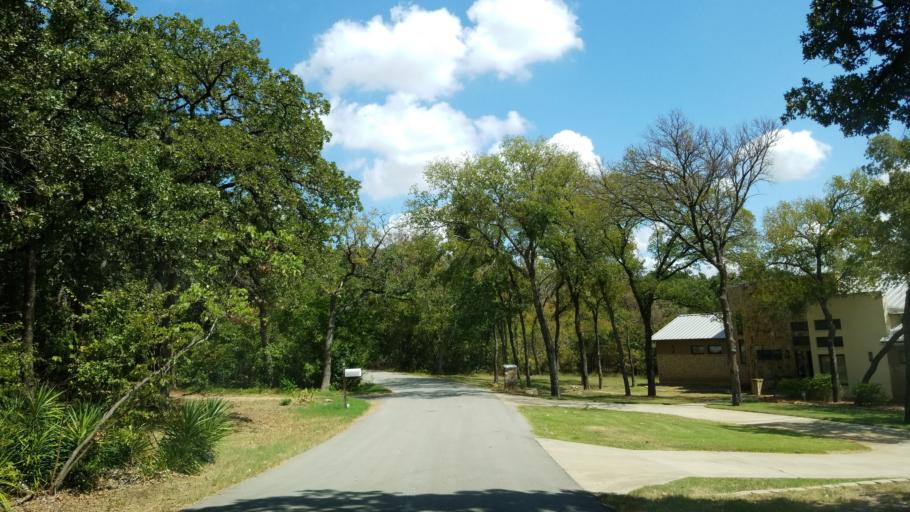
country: US
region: Texas
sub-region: Tarrant County
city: Grapevine
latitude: 32.9072
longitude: -97.1025
